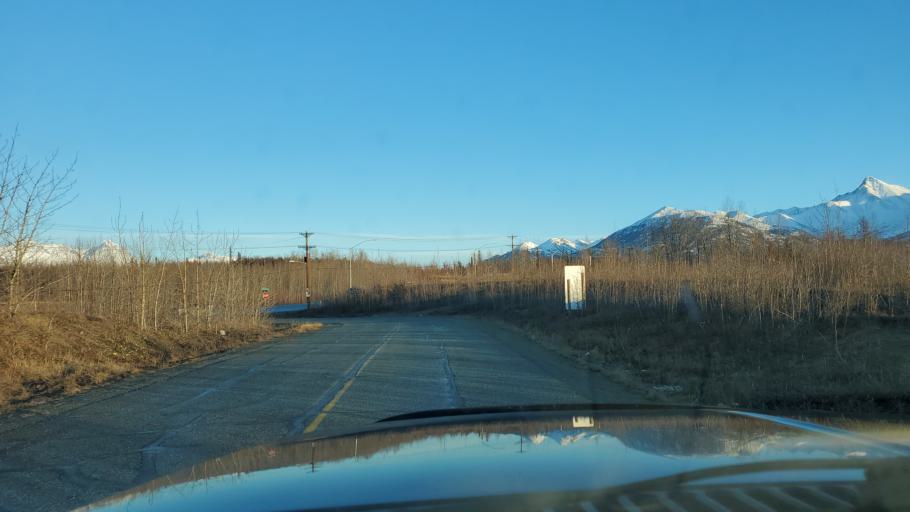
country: US
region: Alaska
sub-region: Matanuska-Susitna Borough
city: Palmer
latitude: 61.5987
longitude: -149.1383
